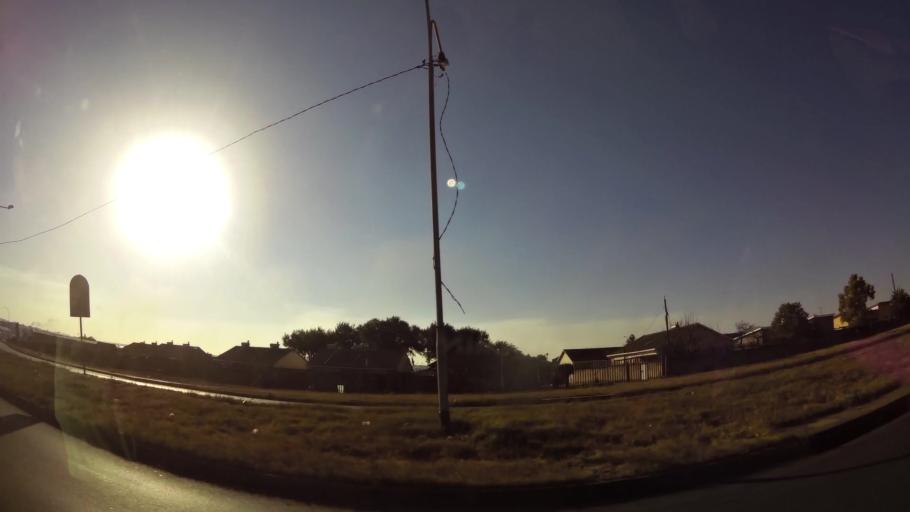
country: ZA
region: Gauteng
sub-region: City of Johannesburg Metropolitan Municipality
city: Johannesburg
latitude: -26.2070
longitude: 27.9624
